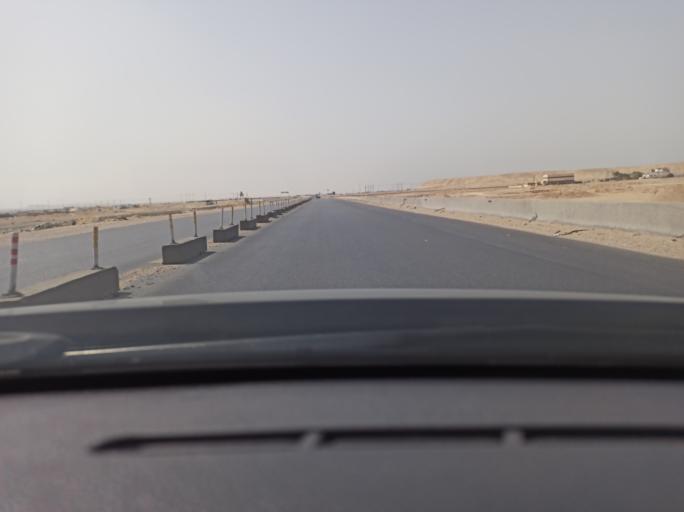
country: EG
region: Muhafazat al Fayyum
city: Al Wasitah
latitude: 29.2895
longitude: 31.2730
